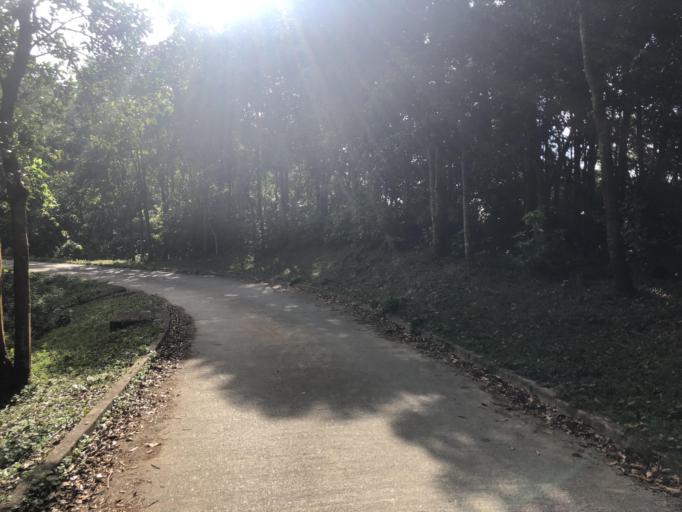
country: HK
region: Tsuen Wan
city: Tsuen Wan
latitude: 22.4045
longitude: 114.0978
